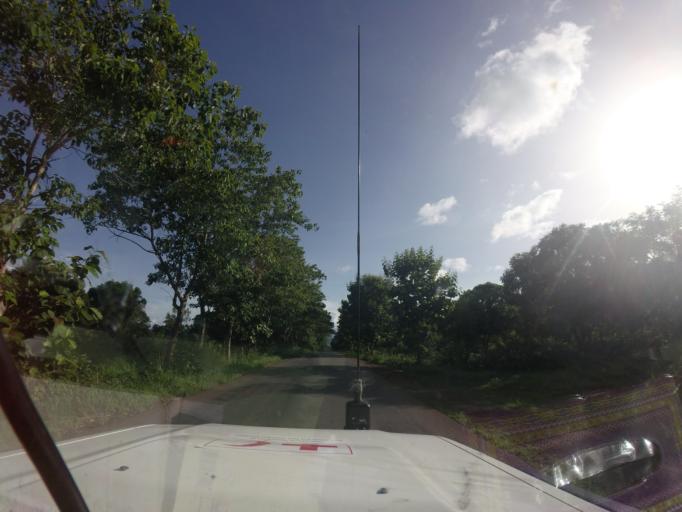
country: GN
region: Kindia
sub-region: Kindia
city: Kindia
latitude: 10.0213
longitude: -12.6786
